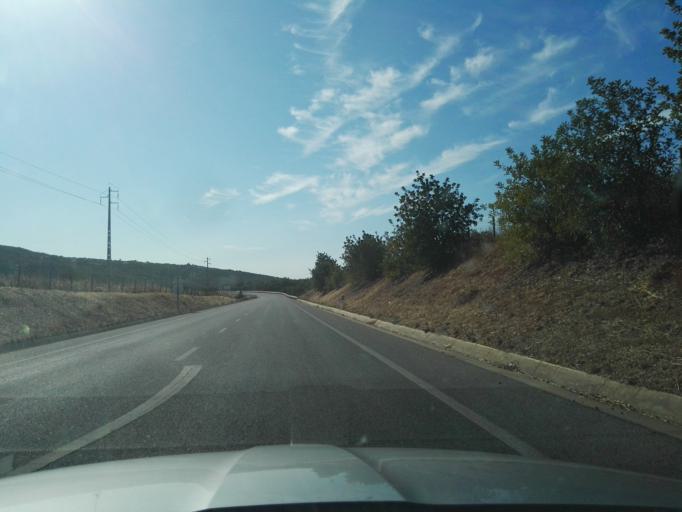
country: PT
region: Faro
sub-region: Sao Bras de Alportel
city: Sao Bras de Alportel
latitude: 37.1468
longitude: -7.8954
